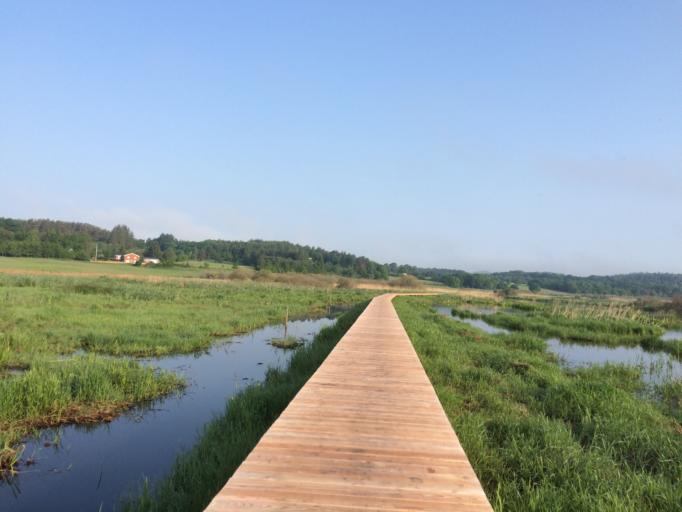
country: DK
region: Central Jutland
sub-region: Silkeborg Kommune
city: Svejbaek
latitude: 56.1947
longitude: 9.6540
